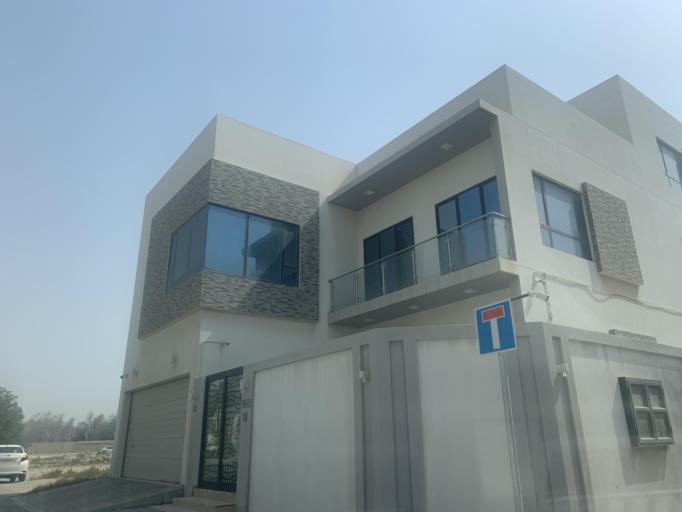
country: BH
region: Manama
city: Jidd Hafs
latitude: 26.2072
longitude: 50.4680
